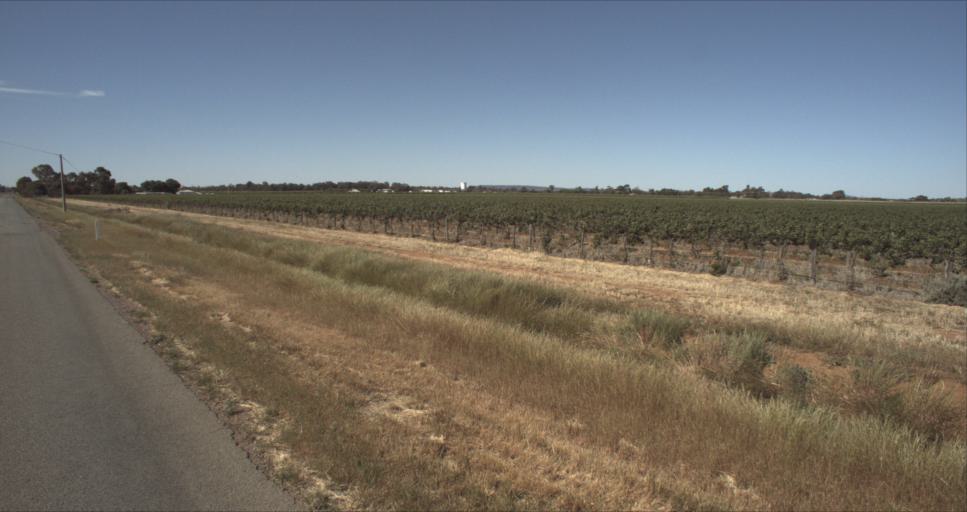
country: AU
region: New South Wales
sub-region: Leeton
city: Leeton
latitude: -34.5724
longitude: 146.3814
